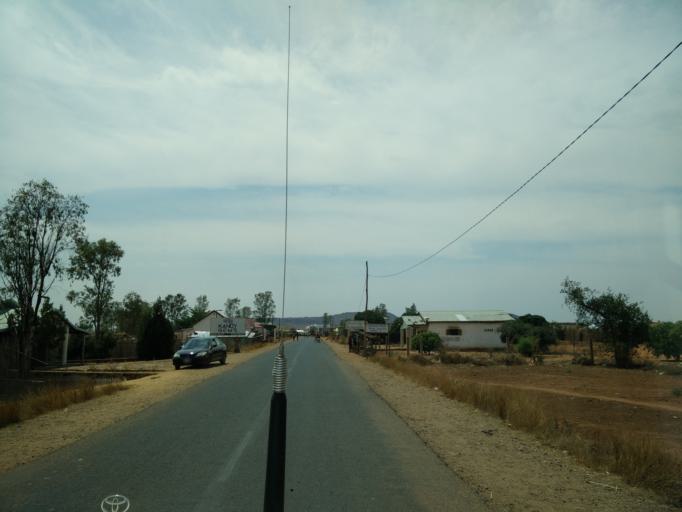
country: MG
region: Ihorombe
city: Ranohira
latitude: -22.7722
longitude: 45.1098
